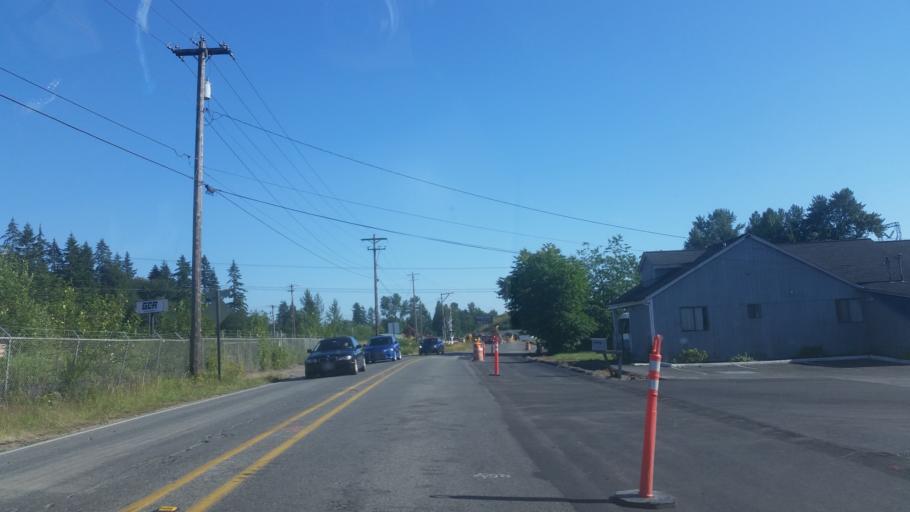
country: US
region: Washington
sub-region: Snohomish County
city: Maltby
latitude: 47.8100
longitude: -122.1101
